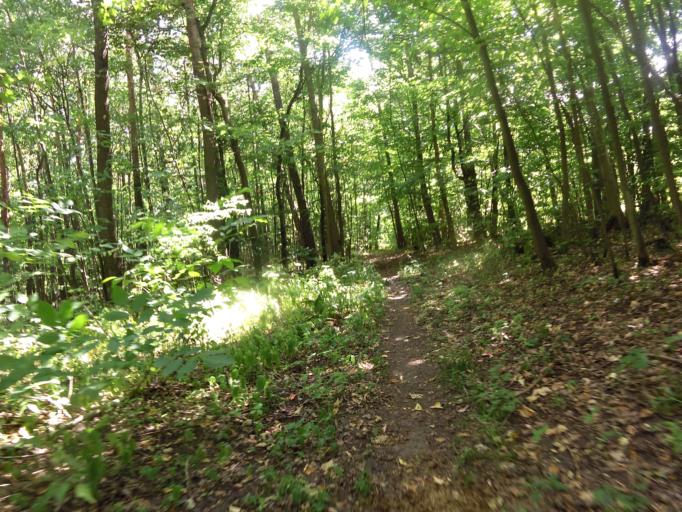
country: DE
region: Bavaria
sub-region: Regierungsbezirk Unterfranken
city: Gadheim
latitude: 49.8174
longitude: 9.9097
